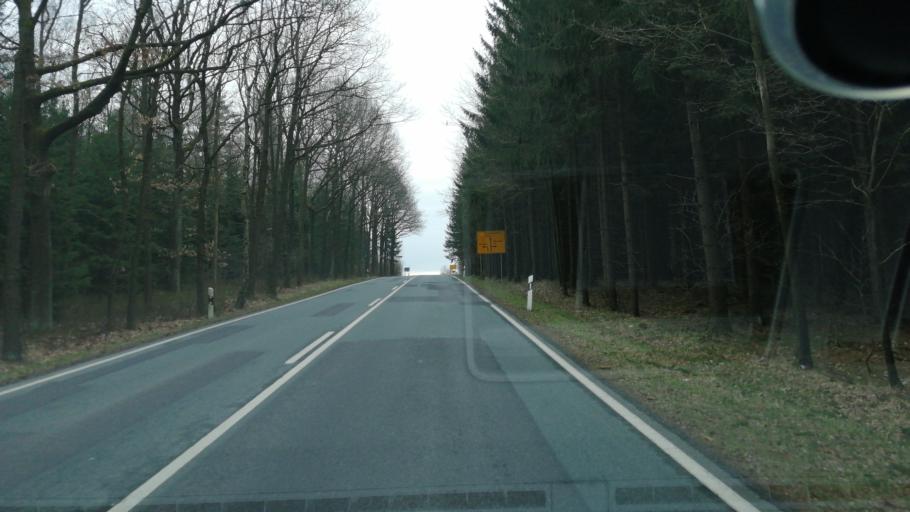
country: DE
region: Saxony
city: Niedercunnersdorf
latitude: 51.0472
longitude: 14.7042
